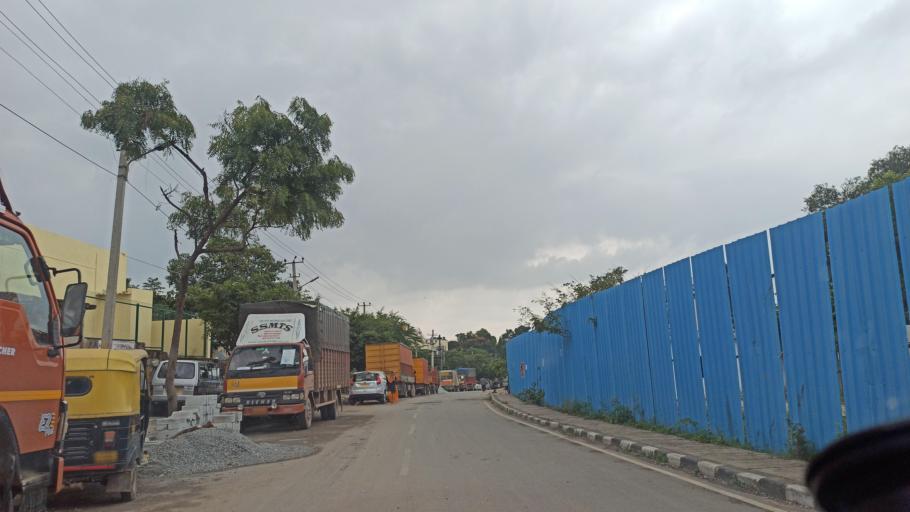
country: IN
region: Karnataka
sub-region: Bangalore Urban
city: Bangalore
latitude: 12.9982
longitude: 77.6761
